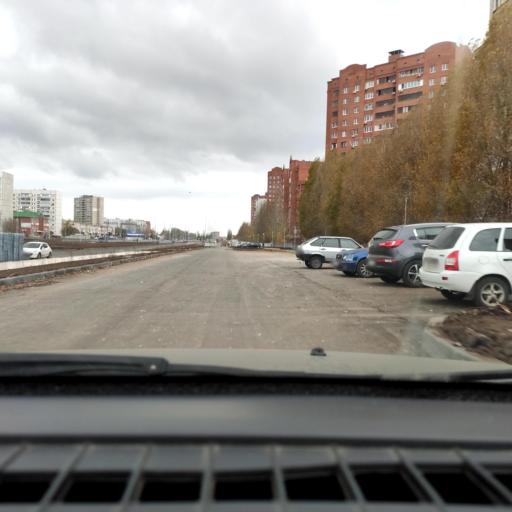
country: RU
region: Samara
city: Tol'yatti
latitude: 53.5473
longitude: 49.3262
